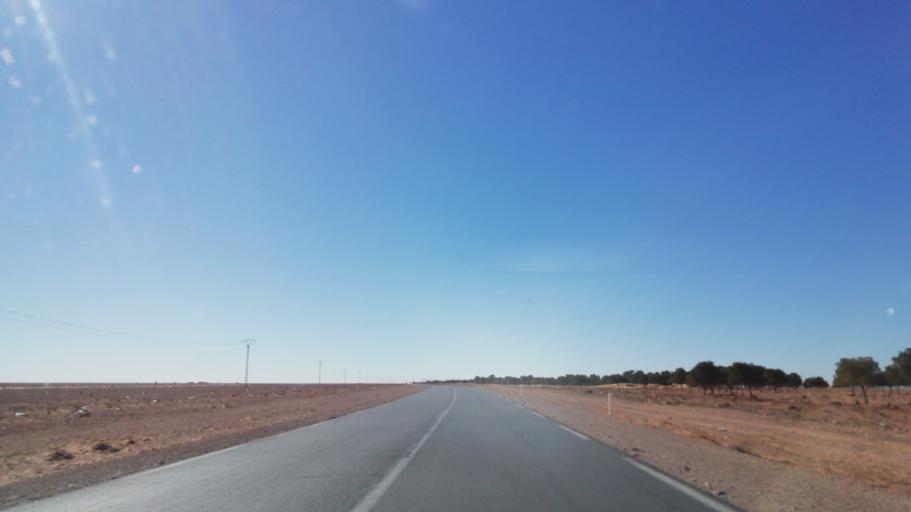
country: DZ
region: Saida
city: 'Ain el Hadjar
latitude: 34.0017
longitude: 0.0441
